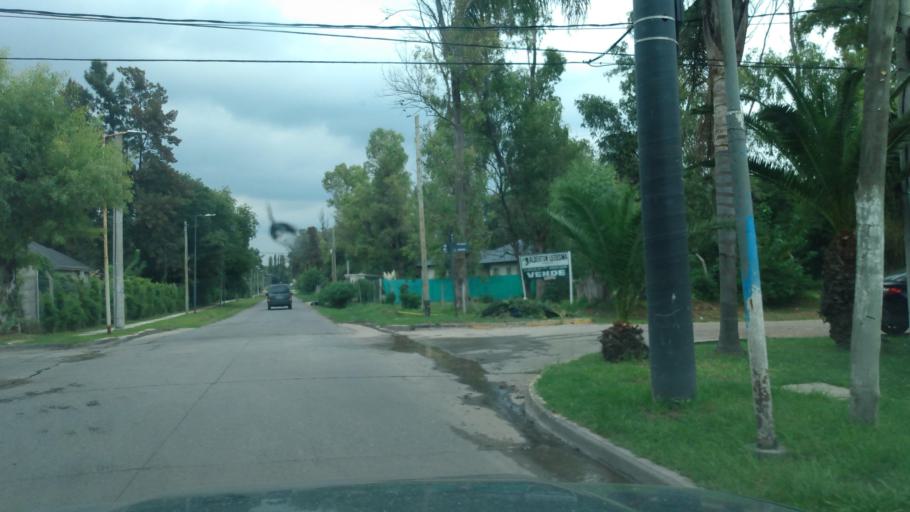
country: AR
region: Buenos Aires
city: Hurlingham
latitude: -34.5730
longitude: -58.6979
